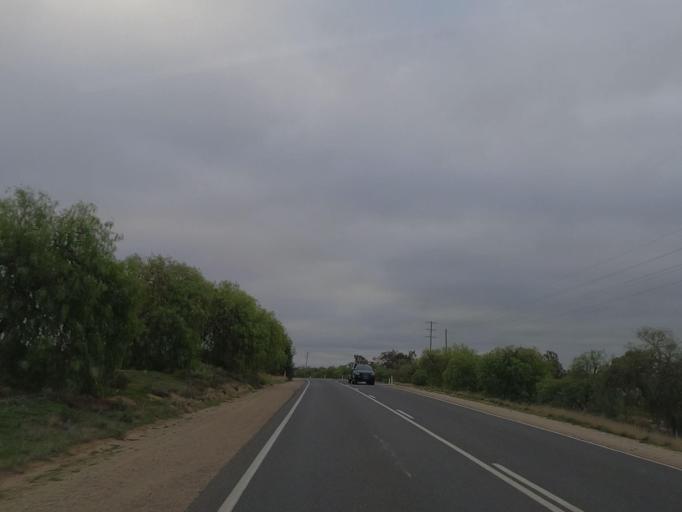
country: AU
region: Victoria
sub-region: Swan Hill
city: Swan Hill
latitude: -35.4465
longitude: 143.6206
